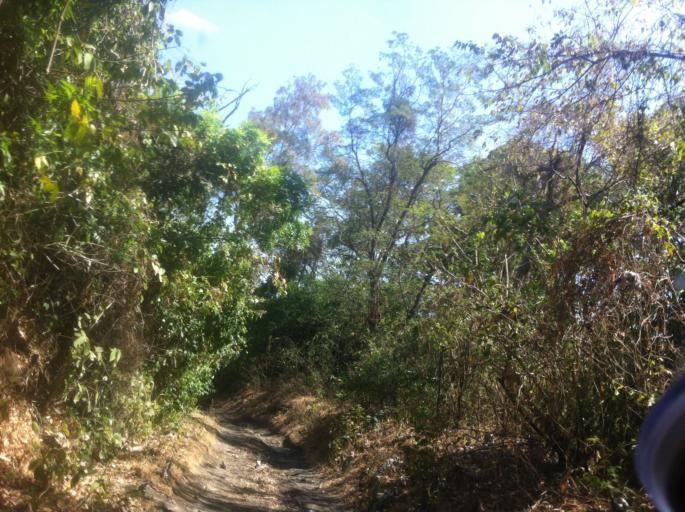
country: NI
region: Chinandega
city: Chichigalpa
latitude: 12.6892
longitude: -87.0279
